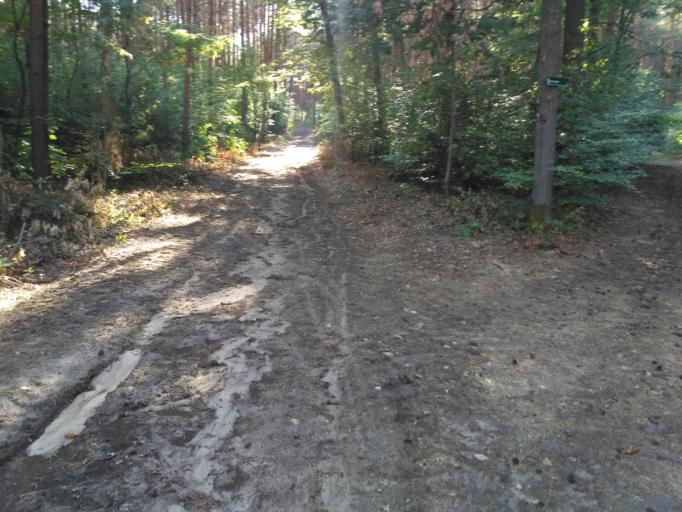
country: DE
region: Saxony
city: Coswig
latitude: 51.1548
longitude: 13.6114
